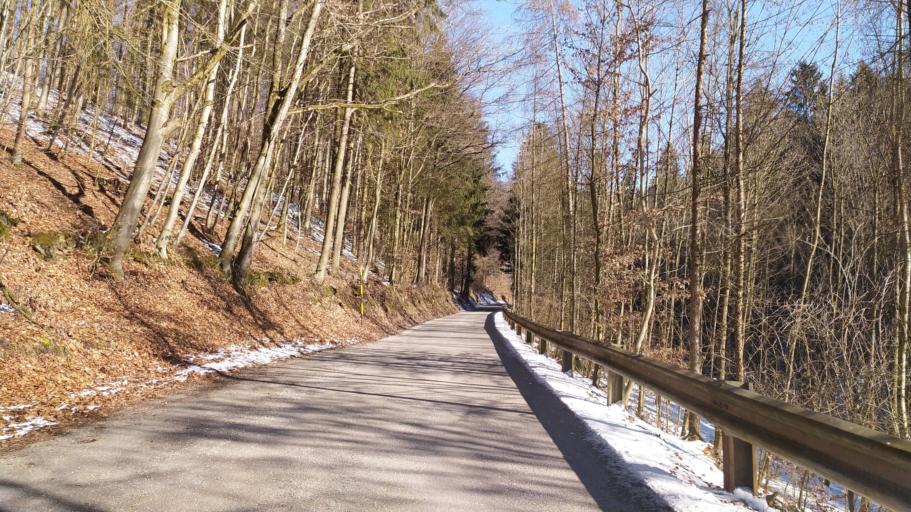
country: AT
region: Upper Austria
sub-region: Politischer Bezirk Urfahr-Umgebung
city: Ottensheim
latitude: 48.3329
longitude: 14.2063
